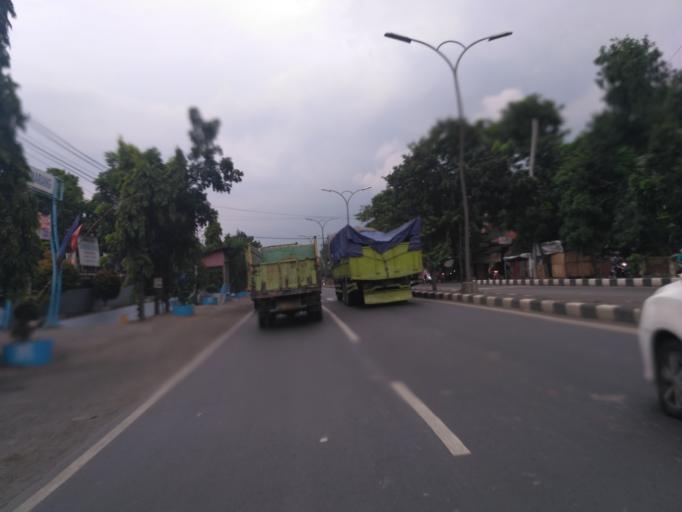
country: ID
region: Central Java
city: Semarang
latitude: -6.9715
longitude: 110.2928
